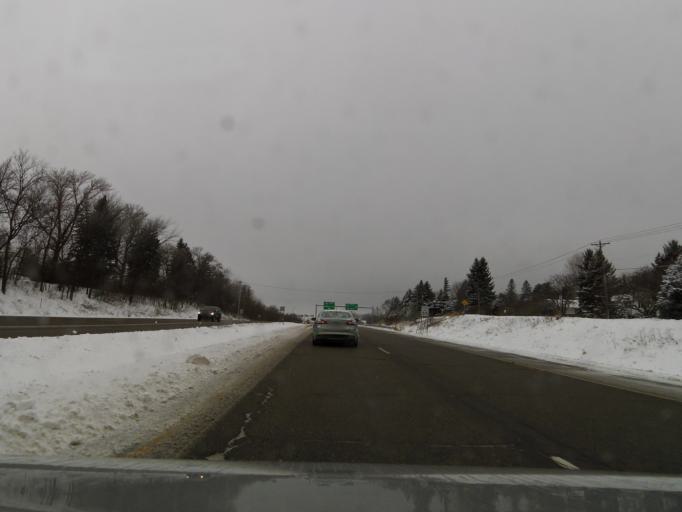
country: US
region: Minnesota
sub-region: Dakota County
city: Mendota Heights
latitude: 44.8839
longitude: -93.1311
